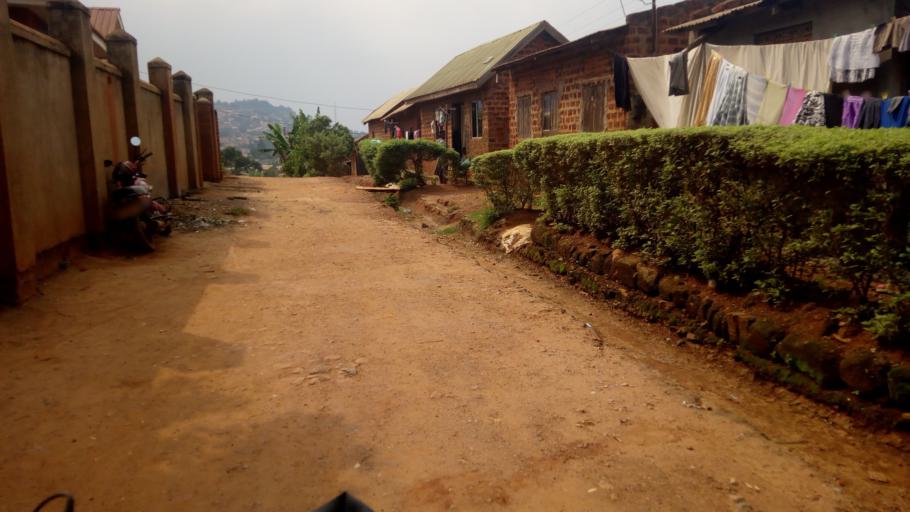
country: UG
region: Central Region
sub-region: Wakiso District
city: Kireka
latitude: 0.3239
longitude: 32.6553
